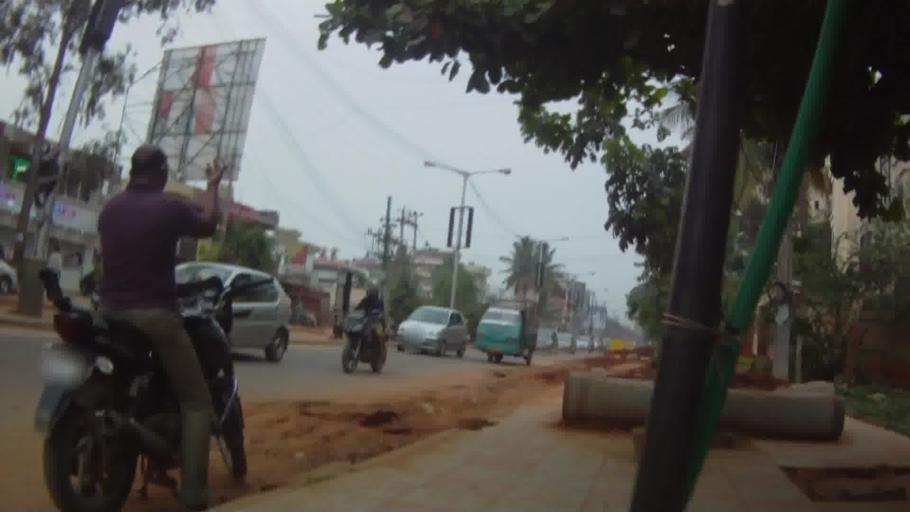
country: IN
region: Karnataka
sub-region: Bangalore Rural
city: Hoskote
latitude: 12.9570
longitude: 77.7426
